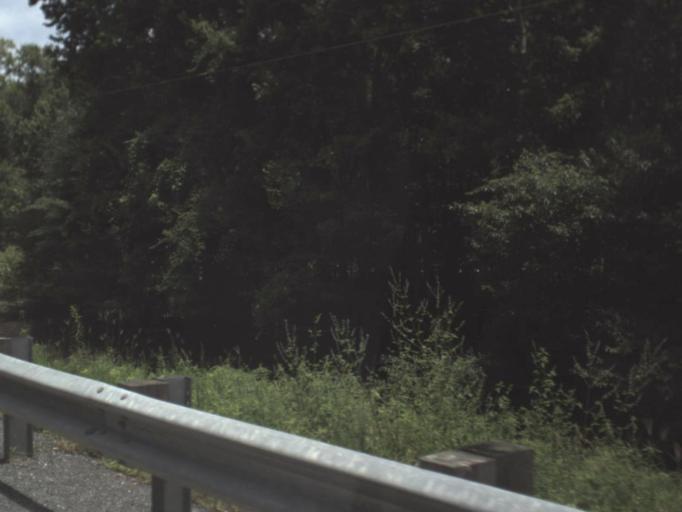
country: US
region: Florida
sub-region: Taylor County
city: Steinhatchee
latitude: 29.8439
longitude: -83.3114
